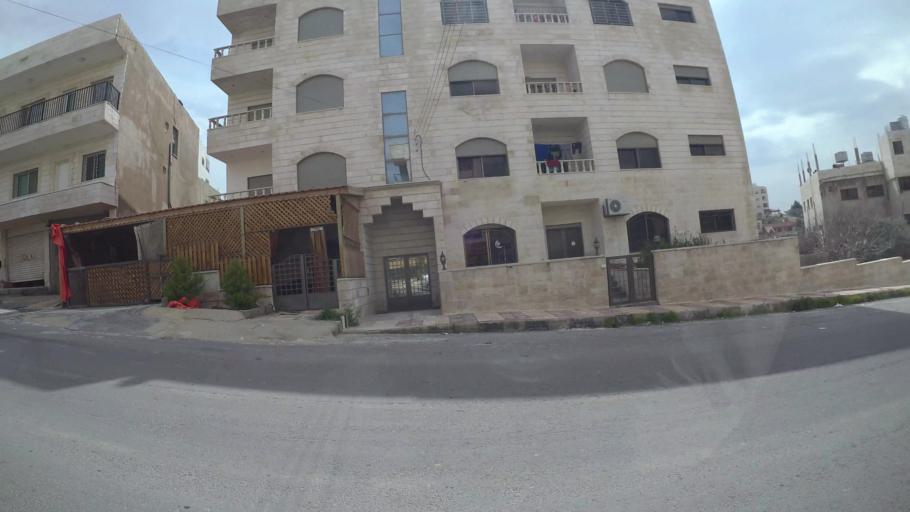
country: JO
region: Amman
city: Umm as Summaq
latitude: 31.9000
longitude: 35.8372
